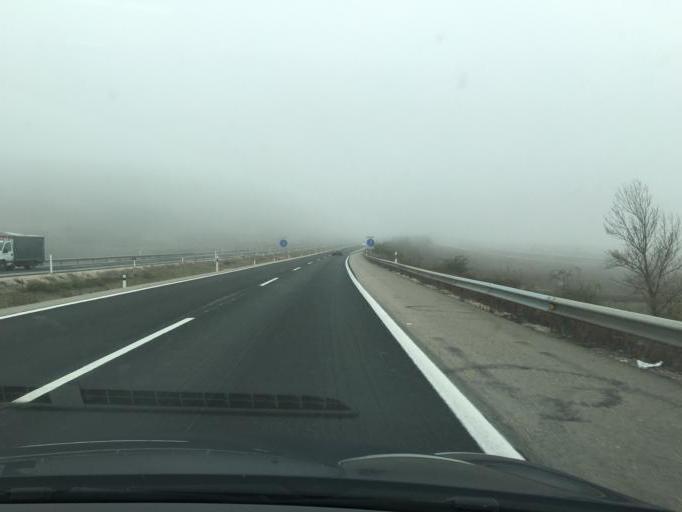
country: ES
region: Castille and Leon
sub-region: Provincia de Burgos
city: Pancorbo
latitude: 42.6218
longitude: -3.1251
